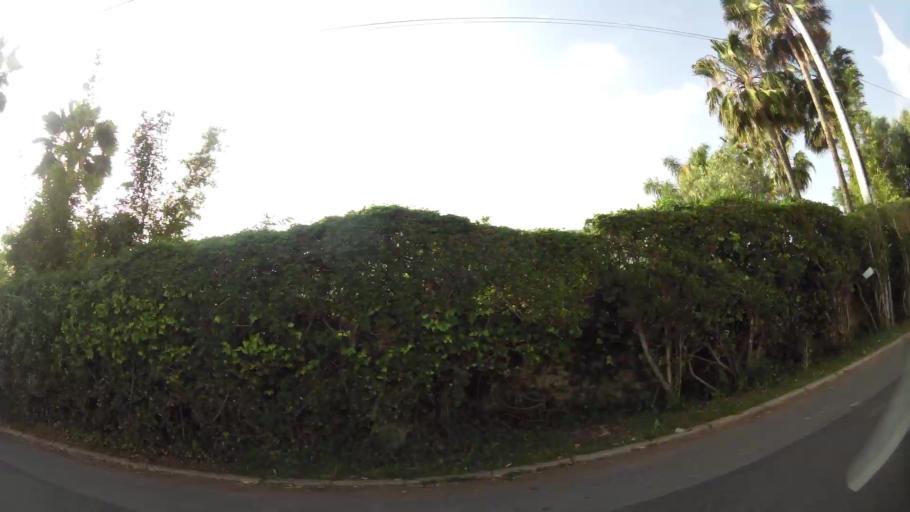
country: MA
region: Rabat-Sale-Zemmour-Zaer
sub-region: Rabat
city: Rabat
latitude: 33.9440
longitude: -6.8088
